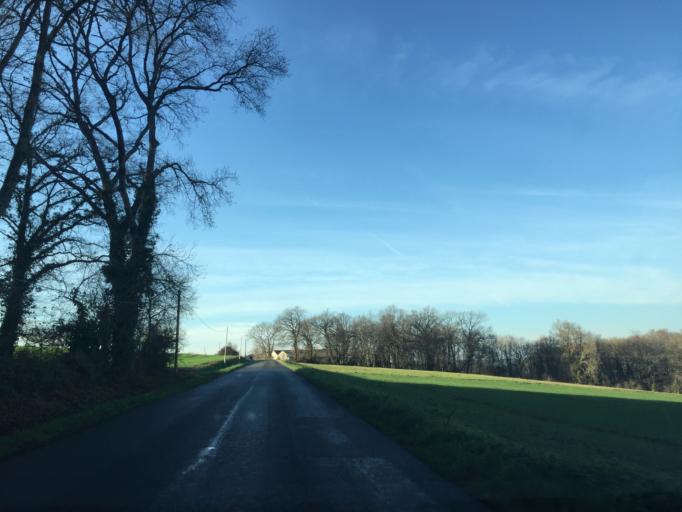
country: FR
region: Aquitaine
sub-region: Departement de la Dordogne
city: Saint-Aulaye
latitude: 45.2520
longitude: 0.2104
